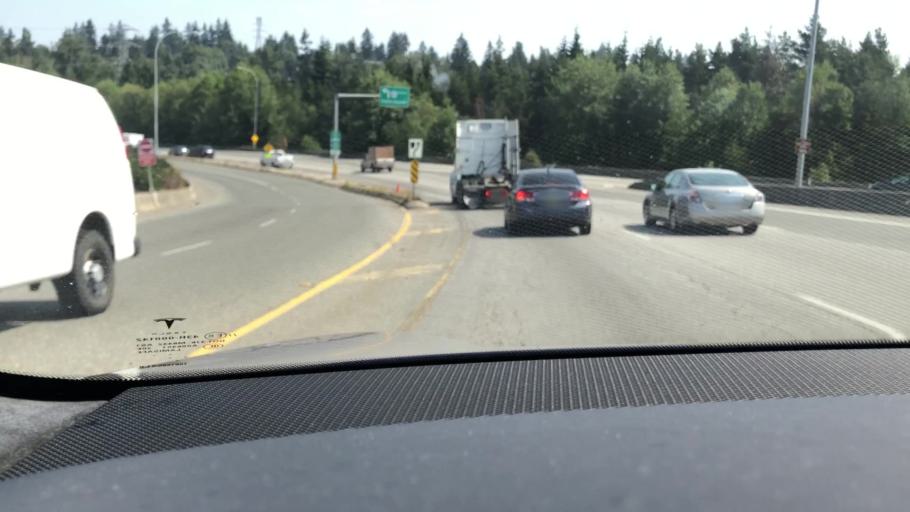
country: CA
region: British Columbia
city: Delta
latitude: 49.1454
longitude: -122.9352
